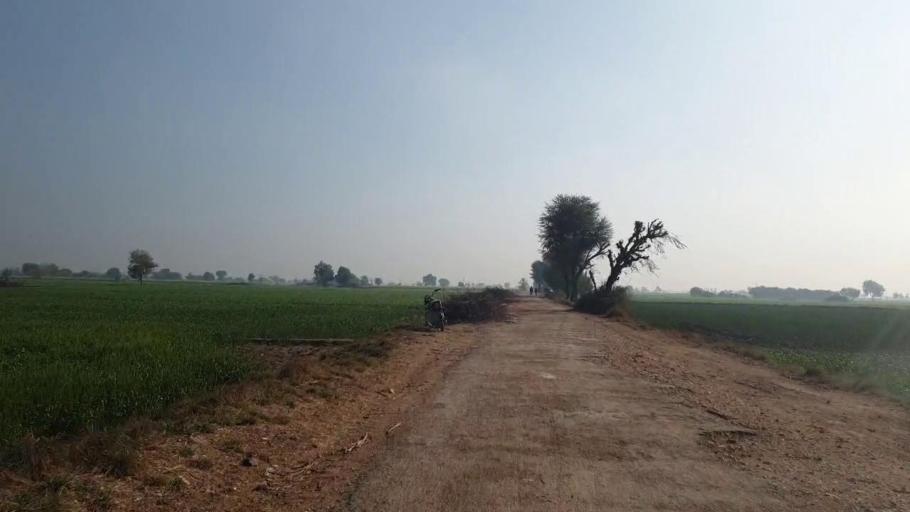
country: PK
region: Sindh
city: Shahdadpur
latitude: 26.0004
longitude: 68.6123
